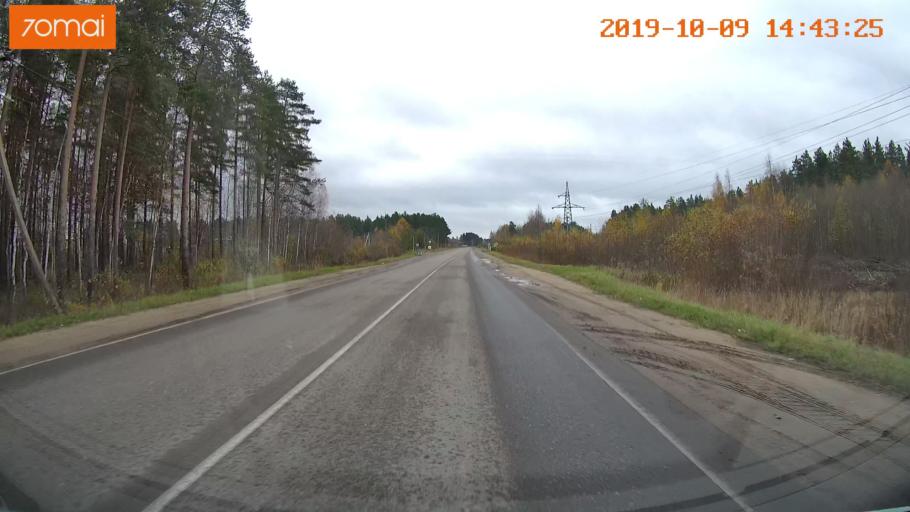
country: RU
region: Kostroma
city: Buy
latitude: 58.4578
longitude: 41.5444
